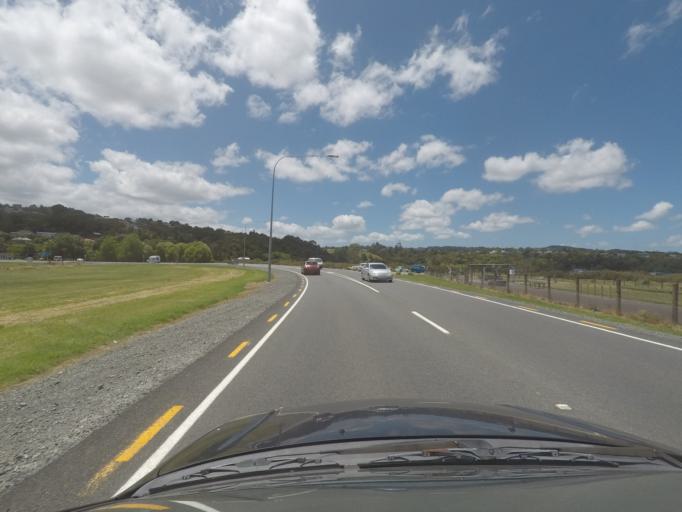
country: NZ
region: Northland
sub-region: Whangarei
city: Whangarei
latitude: -35.7340
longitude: 174.3423
